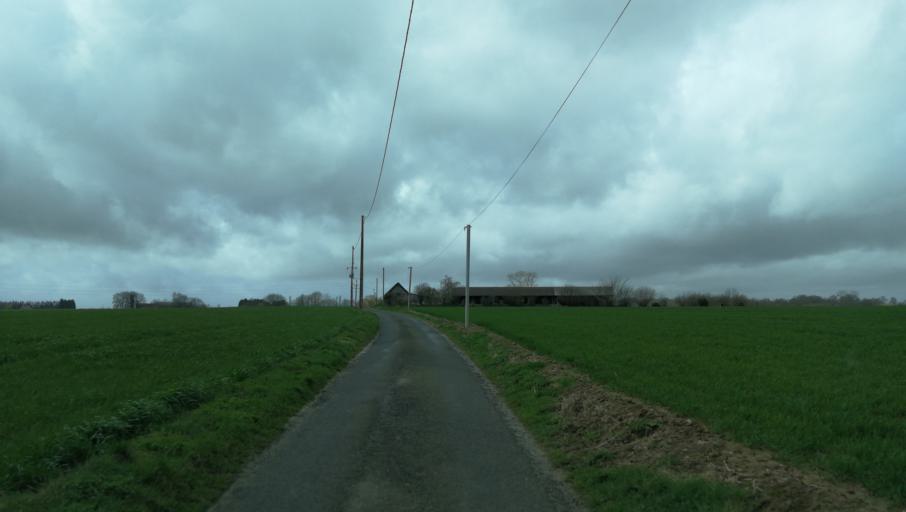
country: FR
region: Haute-Normandie
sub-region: Departement de l'Eure
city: Lieurey
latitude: 49.2329
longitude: 0.5338
